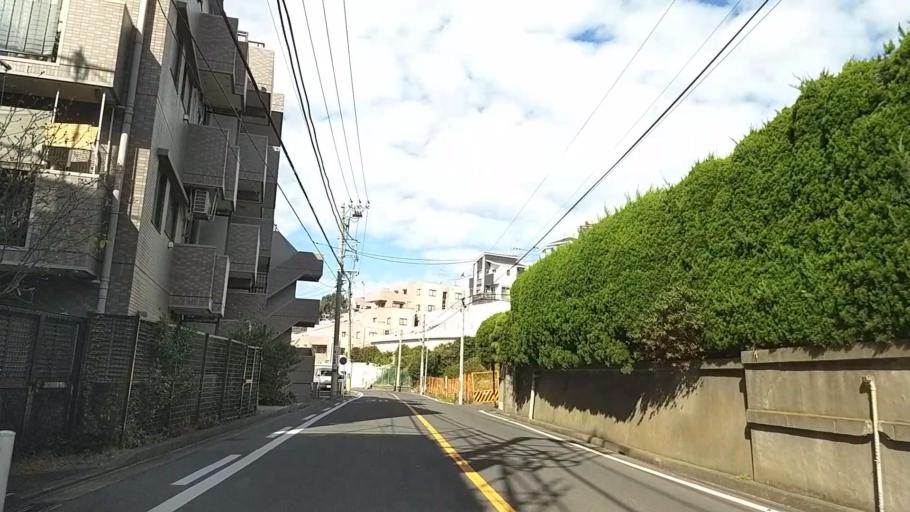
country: JP
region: Kanagawa
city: Yokohama
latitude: 35.5030
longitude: 139.6609
